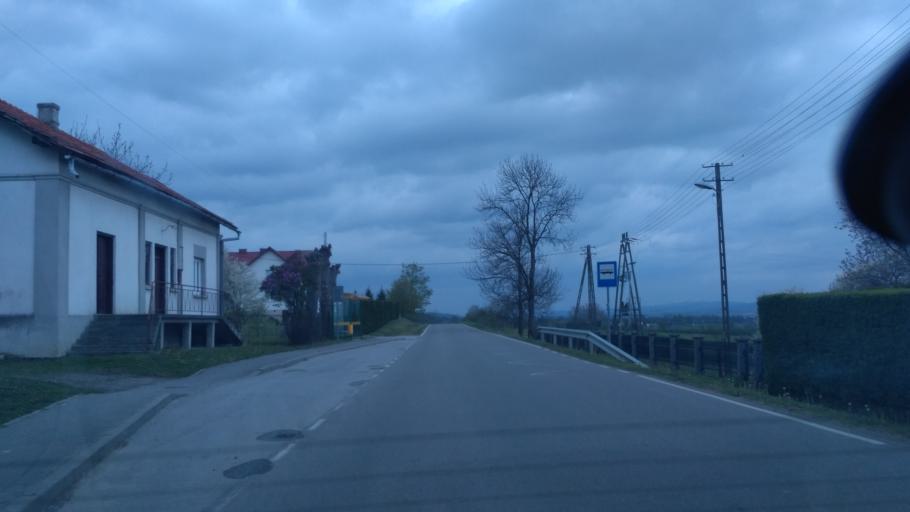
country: PL
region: Subcarpathian Voivodeship
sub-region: Powiat brzozowski
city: Turze Pole
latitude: 49.6394
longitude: 22.0004
